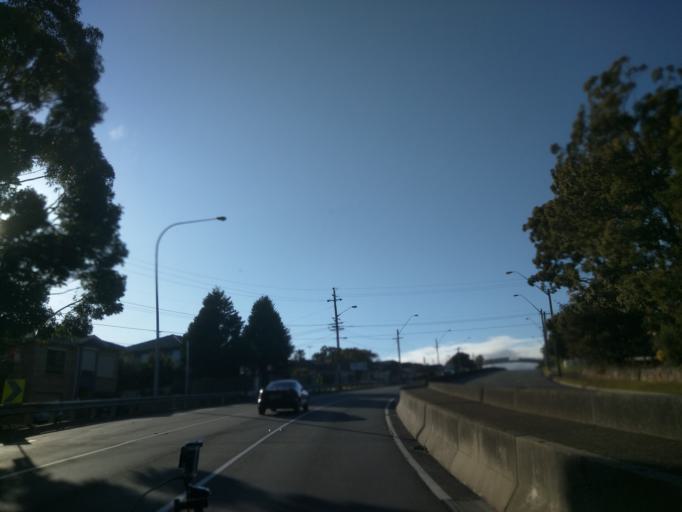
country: AU
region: New South Wales
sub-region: Hurstville
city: Peakhurst
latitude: -33.9605
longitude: 151.0464
